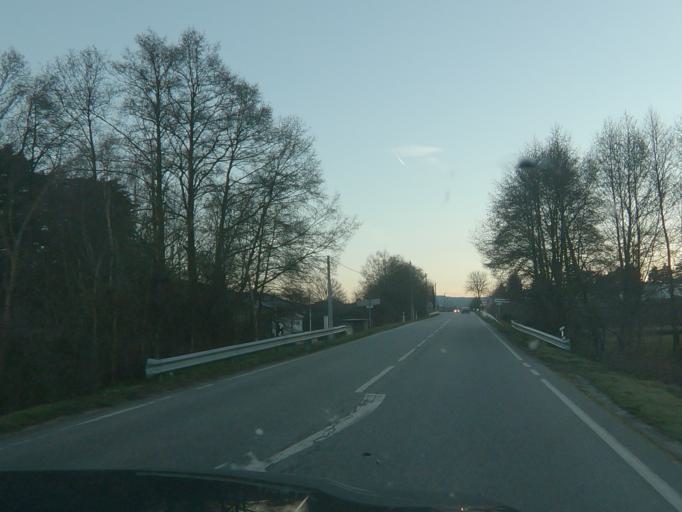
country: PT
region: Vila Real
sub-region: Vila Pouca de Aguiar
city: Vila Pouca de Aguiar
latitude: 41.4401
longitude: -7.6754
